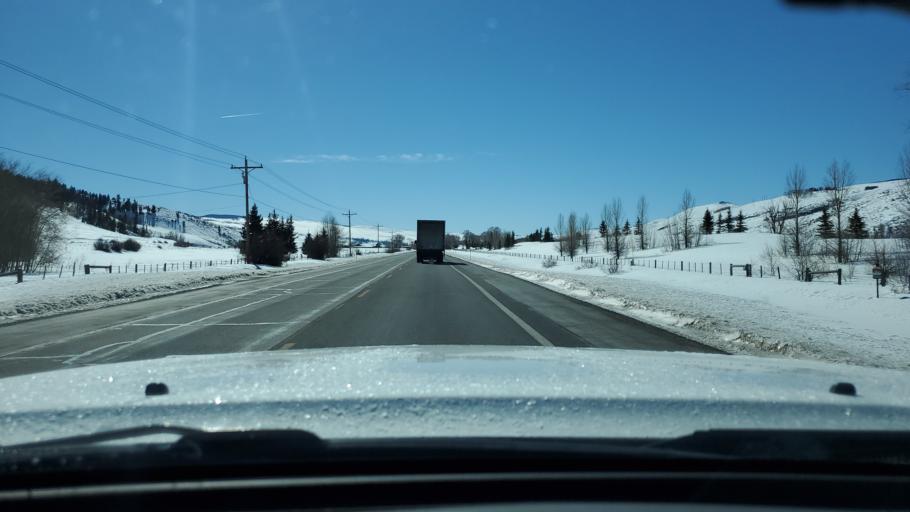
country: US
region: Colorado
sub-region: Gunnison County
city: Crested Butte
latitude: 38.7752
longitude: -106.8682
